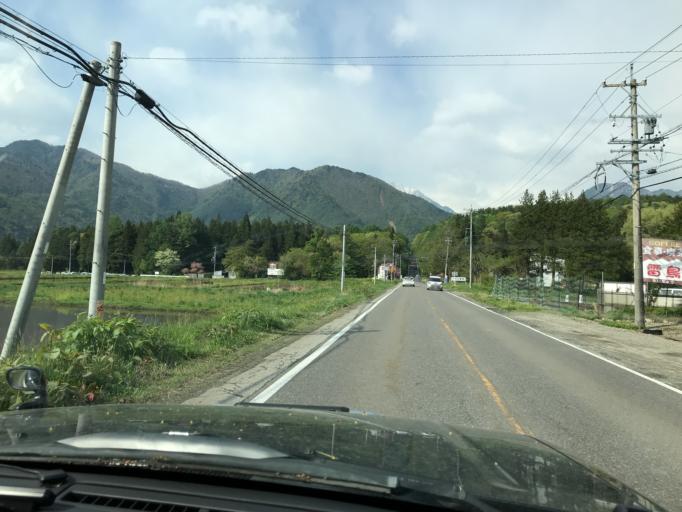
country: JP
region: Nagano
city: Omachi
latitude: 36.5255
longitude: 137.8101
